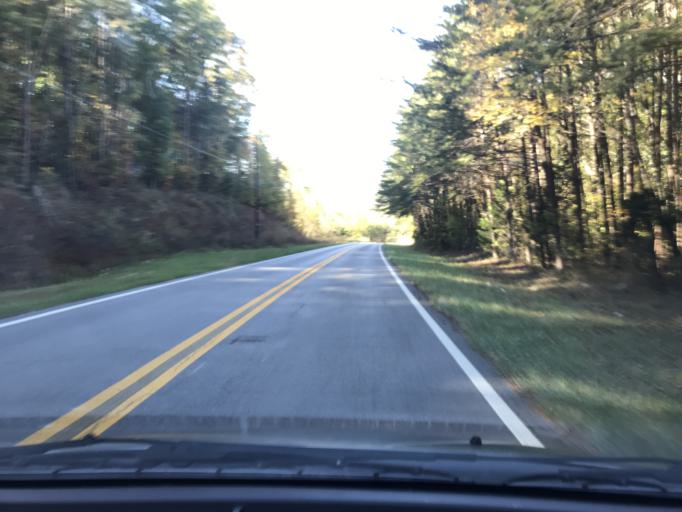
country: US
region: Georgia
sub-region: Dade County
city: Trenton
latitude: 34.8841
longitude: -85.4662
